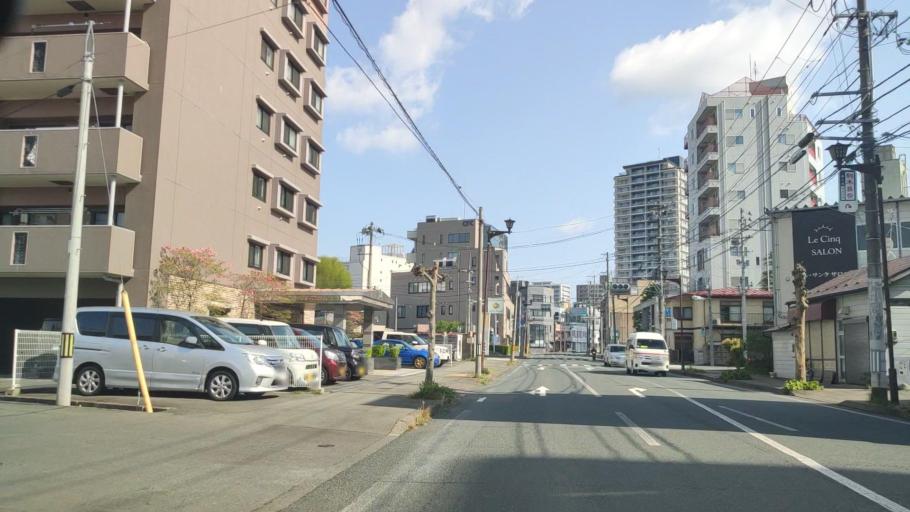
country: JP
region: Iwate
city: Morioka-shi
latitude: 39.6967
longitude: 141.1566
